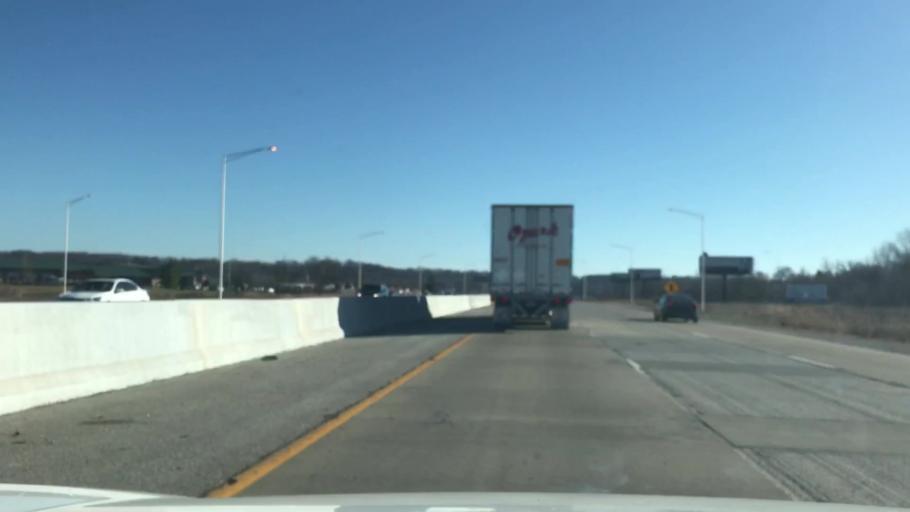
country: US
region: Illinois
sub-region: Saint Clair County
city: Alorton
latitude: 38.5810
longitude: -90.1062
